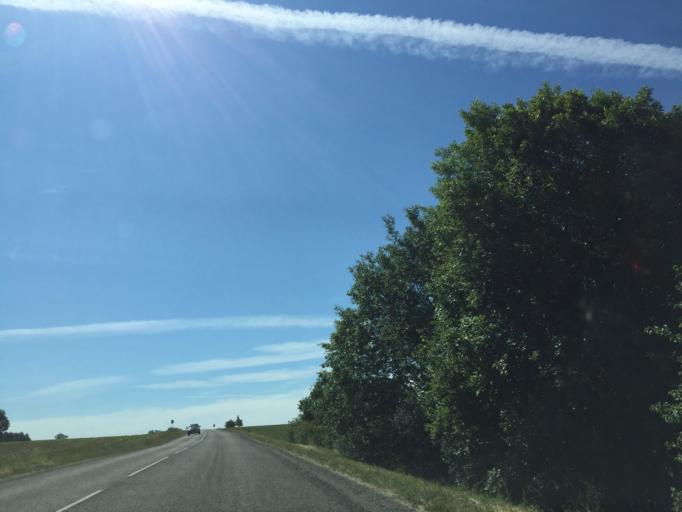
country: LV
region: Aizpute
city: Aizpute
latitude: 56.7060
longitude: 21.7715
